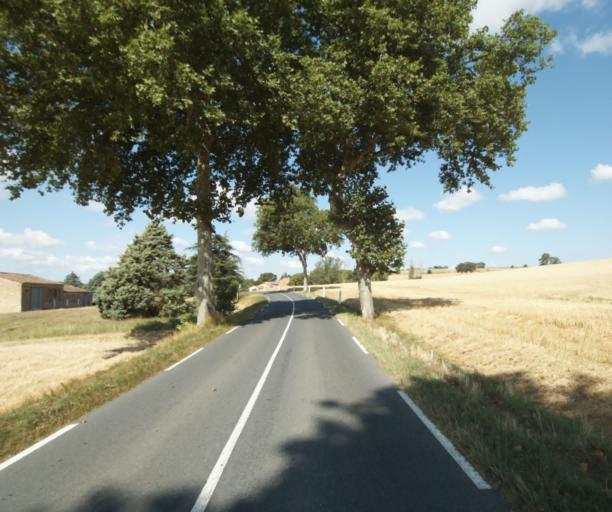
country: FR
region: Midi-Pyrenees
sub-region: Departement de la Haute-Garonne
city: Avignonet-Lauragais
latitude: 43.4463
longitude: 1.8003
